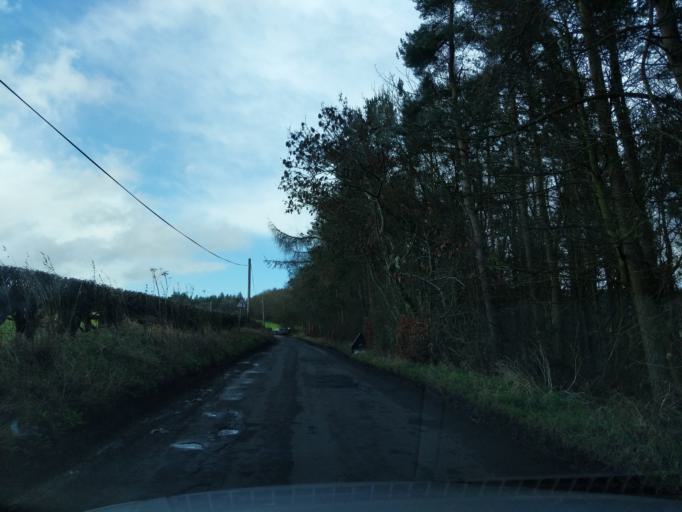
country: GB
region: Scotland
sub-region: Edinburgh
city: Balerno
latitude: 55.8752
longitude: -3.3196
